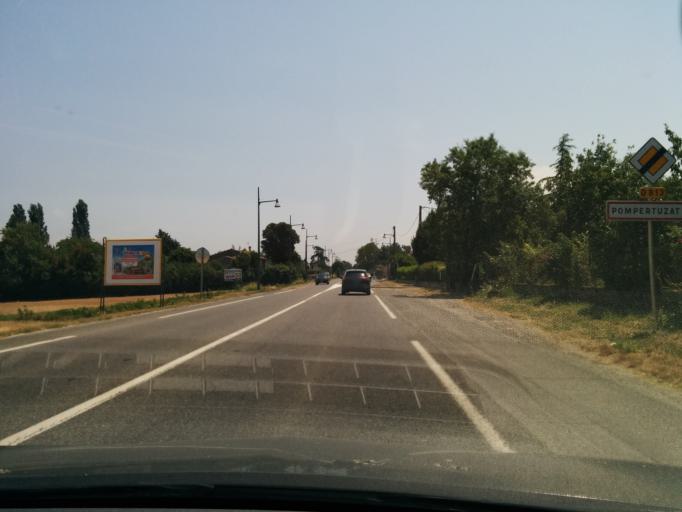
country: FR
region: Midi-Pyrenees
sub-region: Departement de la Haute-Garonne
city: Pompertuzat
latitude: 43.4977
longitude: 1.5170
